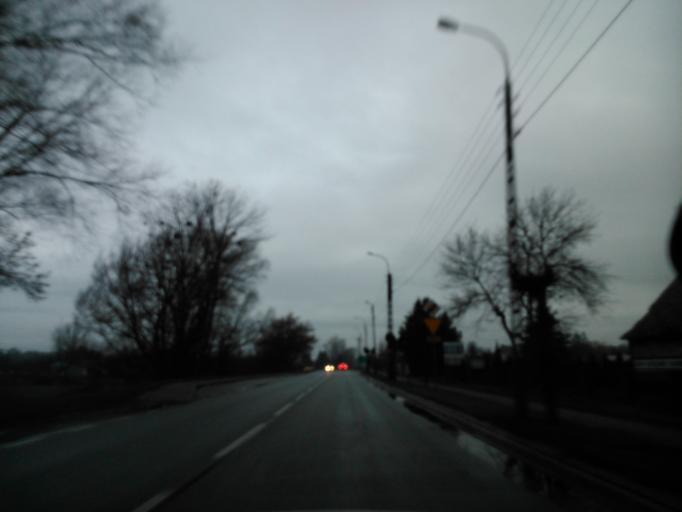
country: PL
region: Lublin Voivodeship
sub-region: Powiat krasnicki
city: Krasnik
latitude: 50.9173
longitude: 22.2409
